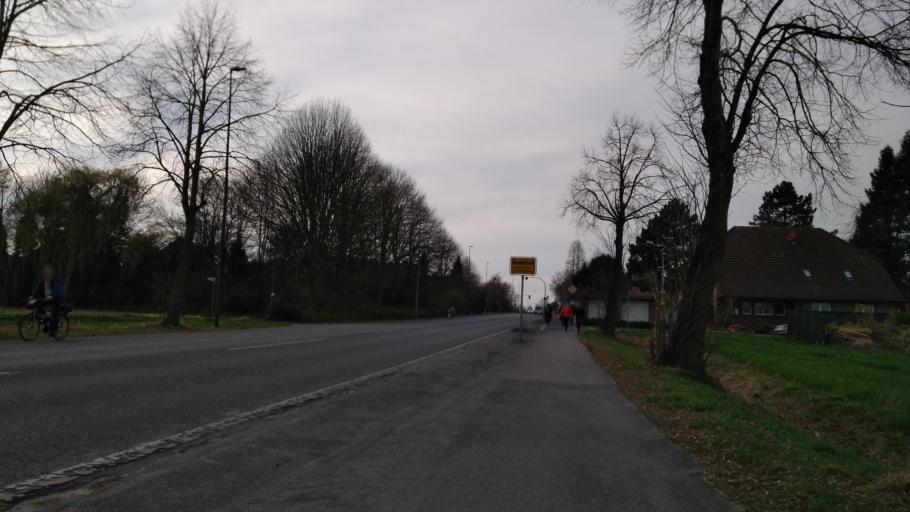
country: DE
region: North Rhine-Westphalia
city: Herten
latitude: 51.5970
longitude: 7.1075
